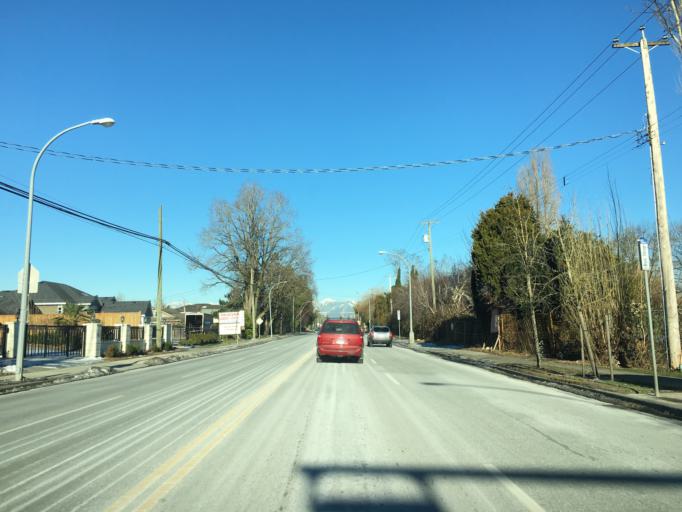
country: CA
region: British Columbia
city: Richmond
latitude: 49.1509
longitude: -123.0918
